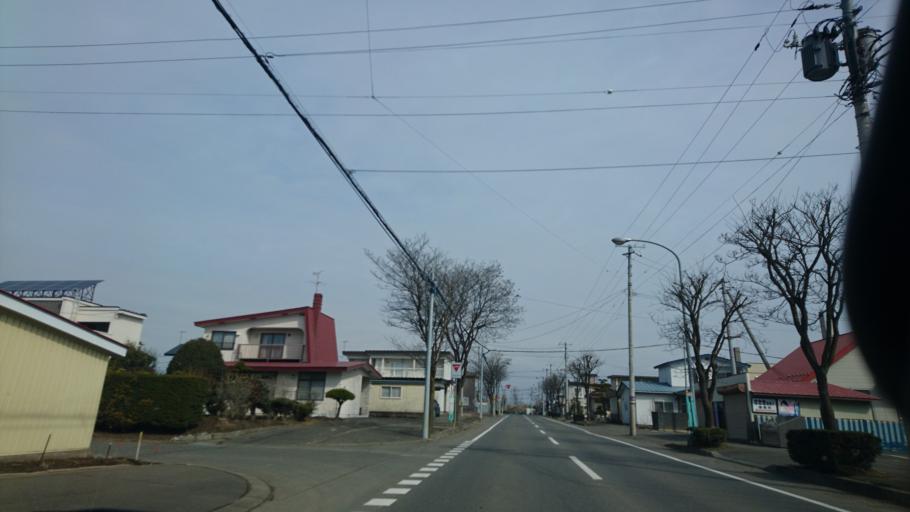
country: JP
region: Hokkaido
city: Otofuke
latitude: 42.9914
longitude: 143.2099
